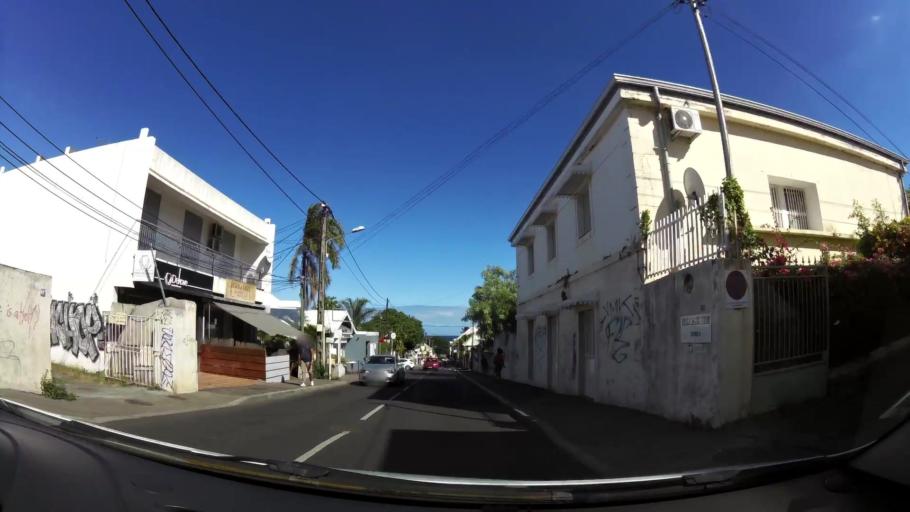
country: RE
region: Reunion
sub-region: Reunion
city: Saint-Pierre
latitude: -21.3395
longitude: 55.4793
